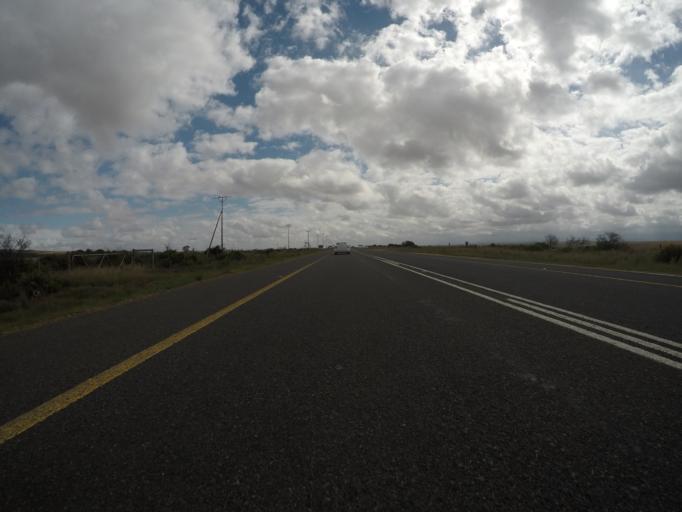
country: ZA
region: Western Cape
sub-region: Eden District Municipality
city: Riversdale
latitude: -34.1703
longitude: 21.3258
